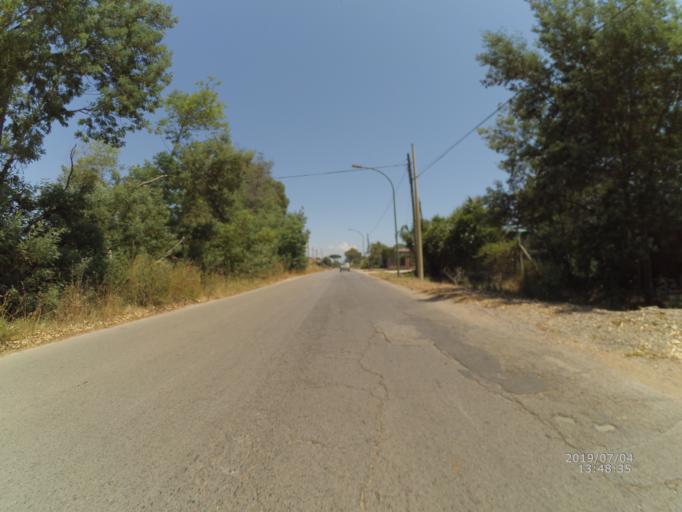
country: IT
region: Latium
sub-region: Provincia di Latina
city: San Felice Circeo
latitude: 41.2849
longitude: 13.1062
